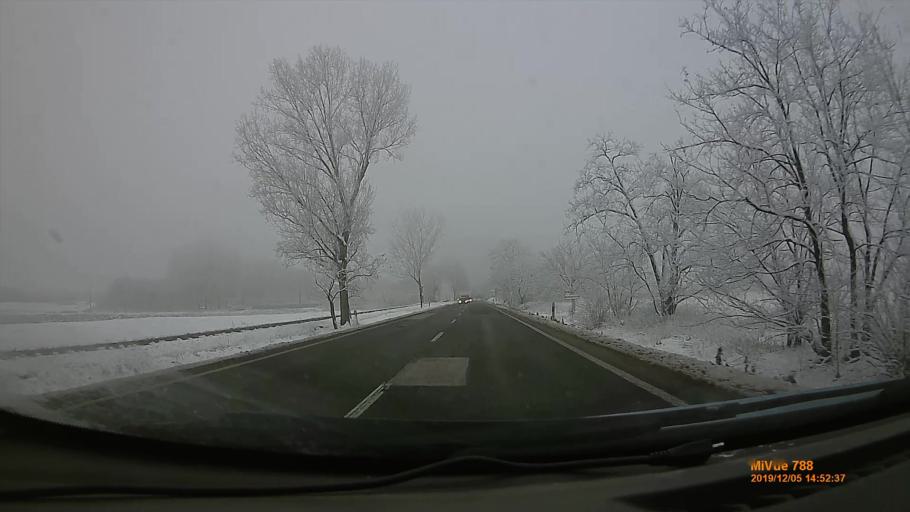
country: HU
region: Szabolcs-Szatmar-Bereg
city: Nyirtelek
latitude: 48.0030
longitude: 21.6424
